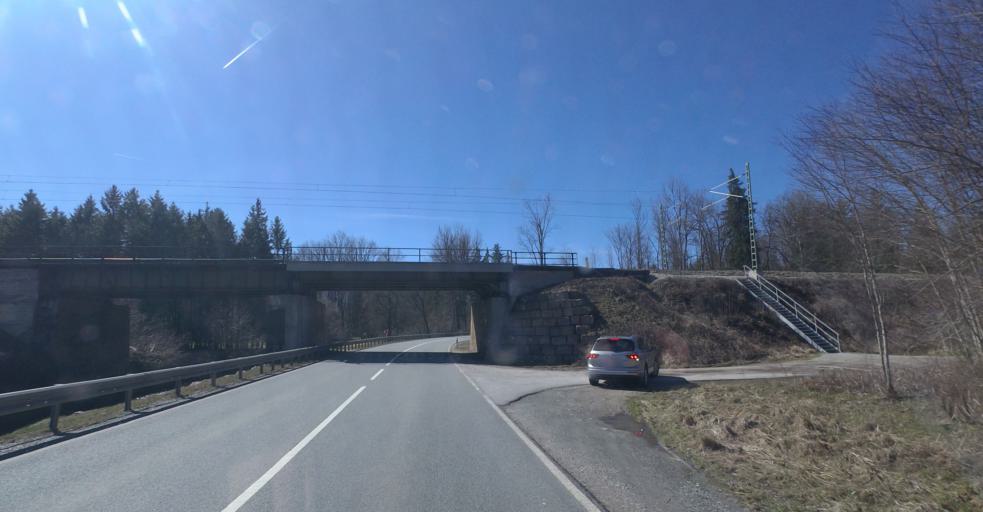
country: DE
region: Bavaria
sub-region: Upper Bavaria
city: Ubersee
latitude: 47.8220
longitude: 12.5109
